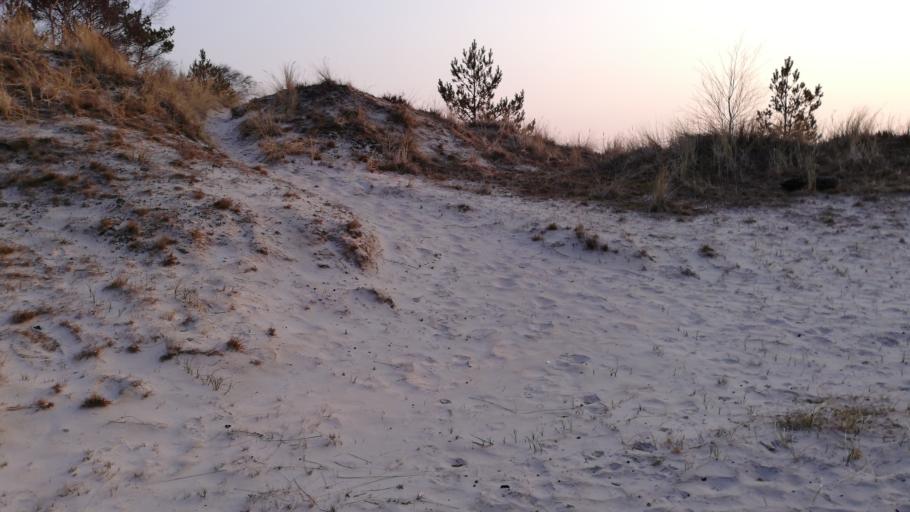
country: SE
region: Skane
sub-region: Simrishamns Kommun
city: Simrishamn
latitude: 55.3850
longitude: 14.1956
